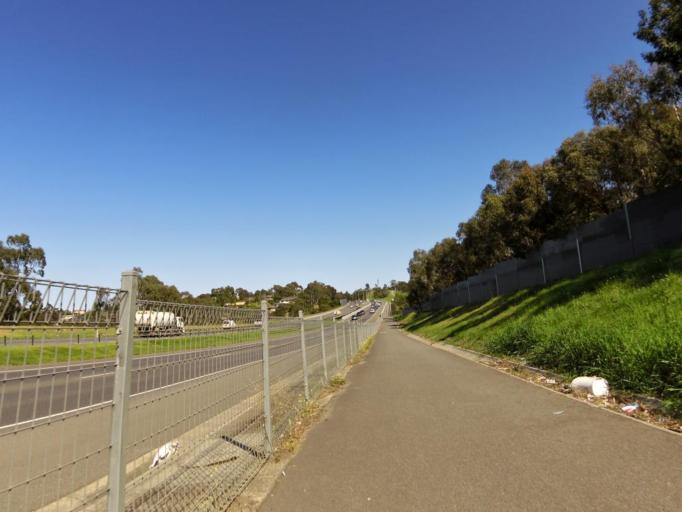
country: AU
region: Victoria
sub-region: Banyule
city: Greensborough
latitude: -37.6920
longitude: 145.1027
